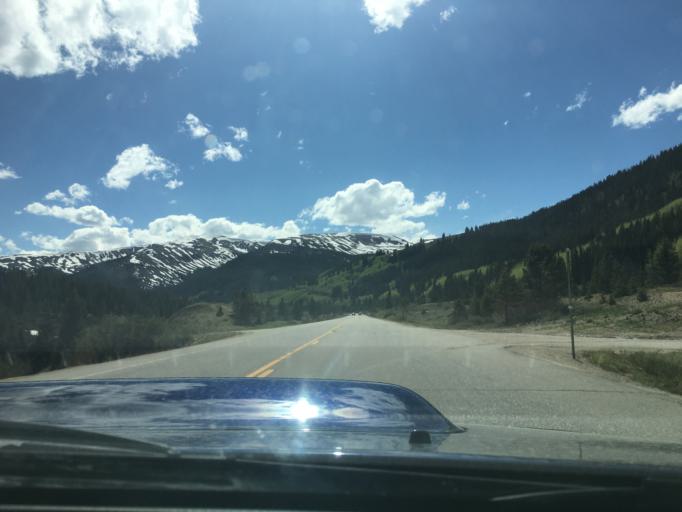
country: US
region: Colorado
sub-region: Lake County
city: Leadville
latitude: 39.3608
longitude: -106.1966
